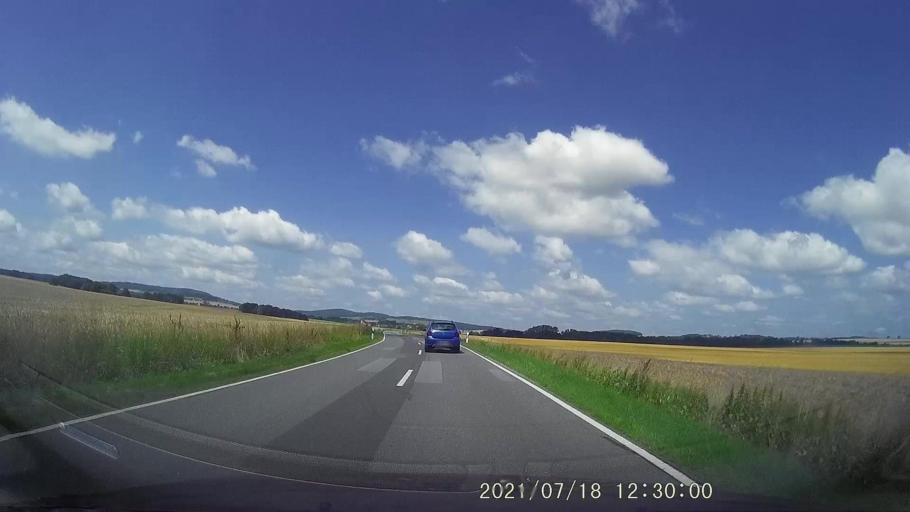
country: DE
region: Saxony
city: Markersdorf
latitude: 51.1696
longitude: 14.9149
